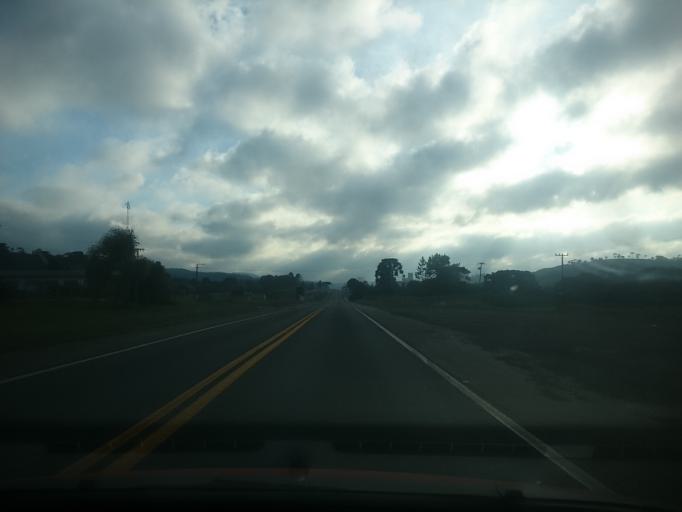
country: BR
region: Santa Catarina
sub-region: Lages
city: Lages
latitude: -28.0098
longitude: -50.5449
